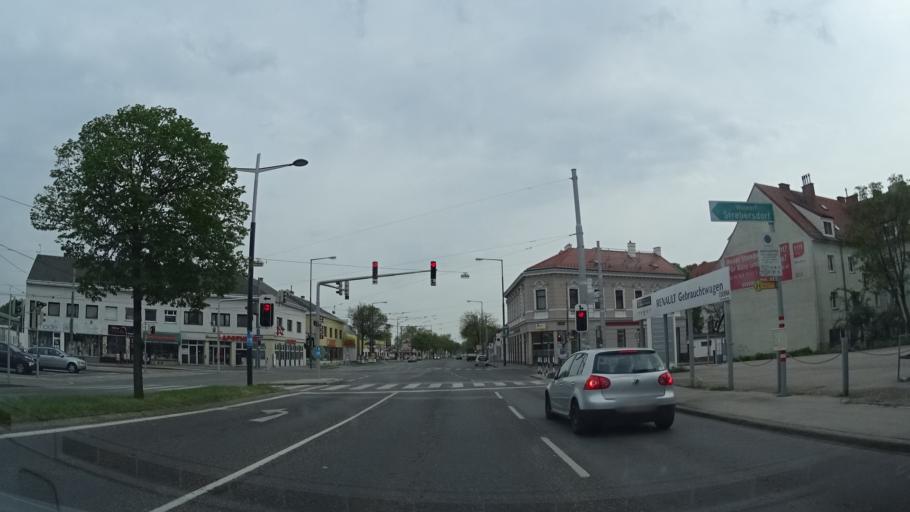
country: AT
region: Lower Austria
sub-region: Politischer Bezirk Korneuburg
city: Langenzersdorf
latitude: 48.2877
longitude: 16.3829
